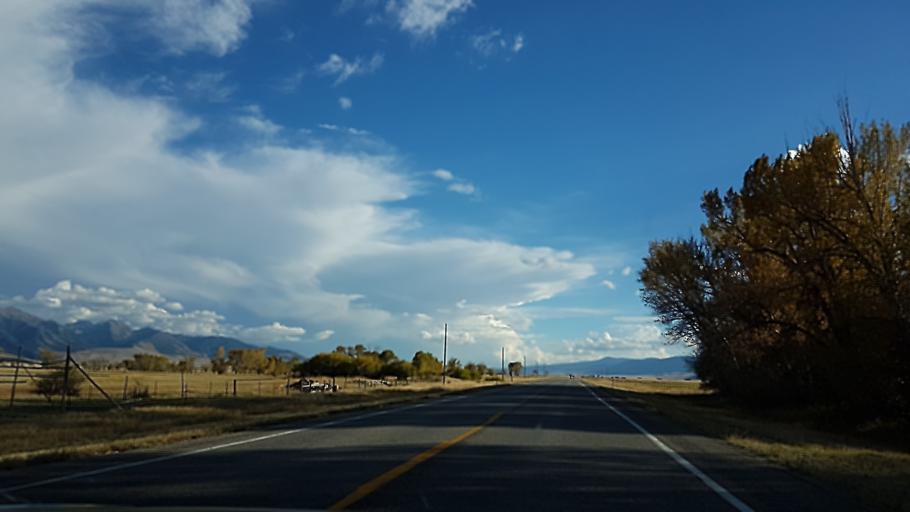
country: US
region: Montana
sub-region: Madison County
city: Virginia City
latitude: 45.2006
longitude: -111.6788
